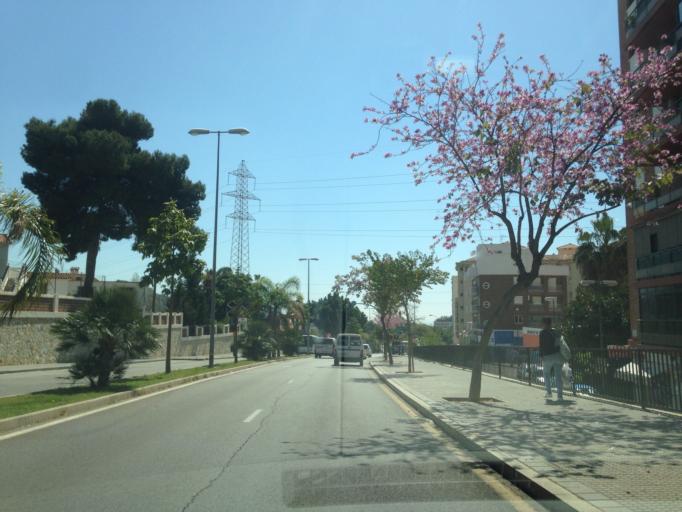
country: ES
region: Andalusia
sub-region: Provincia de Malaga
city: Malaga
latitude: 36.7318
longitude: -4.4704
